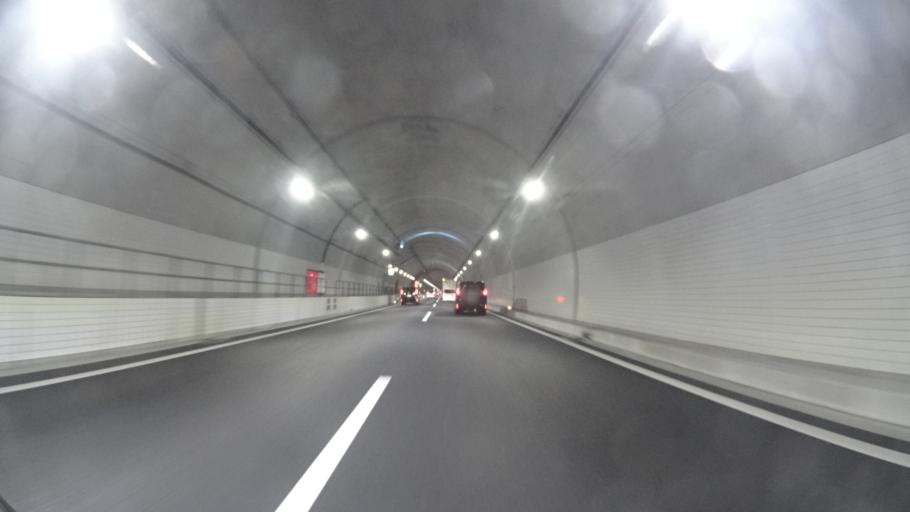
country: JP
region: Mie
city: Komono
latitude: 34.9444
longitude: 136.4468
